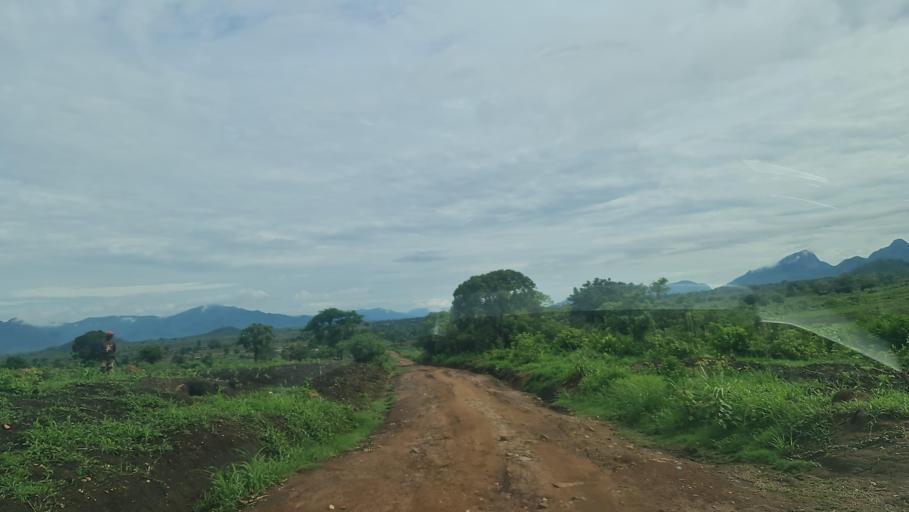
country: MZ
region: Nampula
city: Mutuali
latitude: -15.3047
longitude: 36.7594
